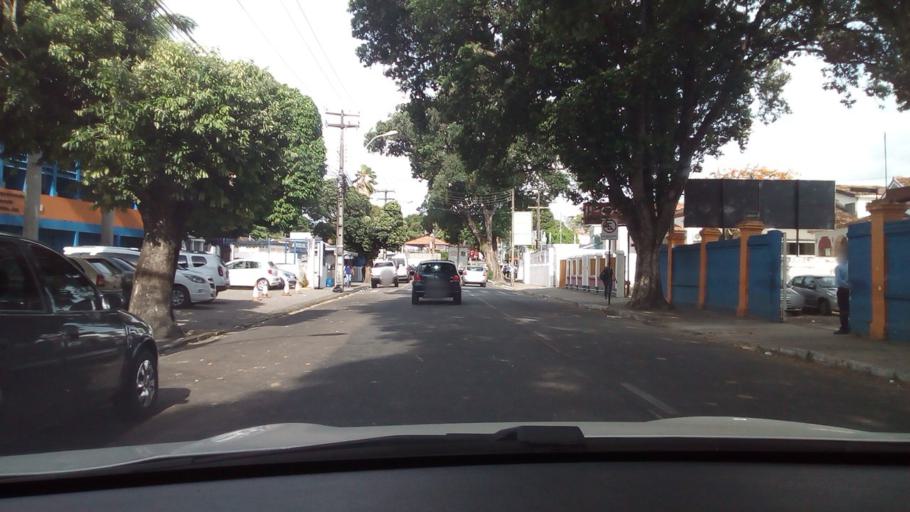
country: BR
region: Paraiba
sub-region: Joao Pessoa
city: Joao Pessoa
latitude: -7.1174
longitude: -34.8732
